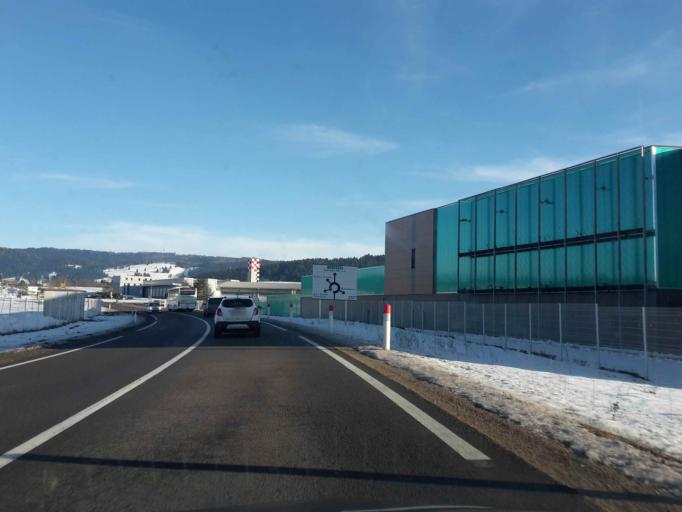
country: FR
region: Franche-Comte
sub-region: Departement du Doubs
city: Pontarlier
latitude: 46.9003
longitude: 6.3321
